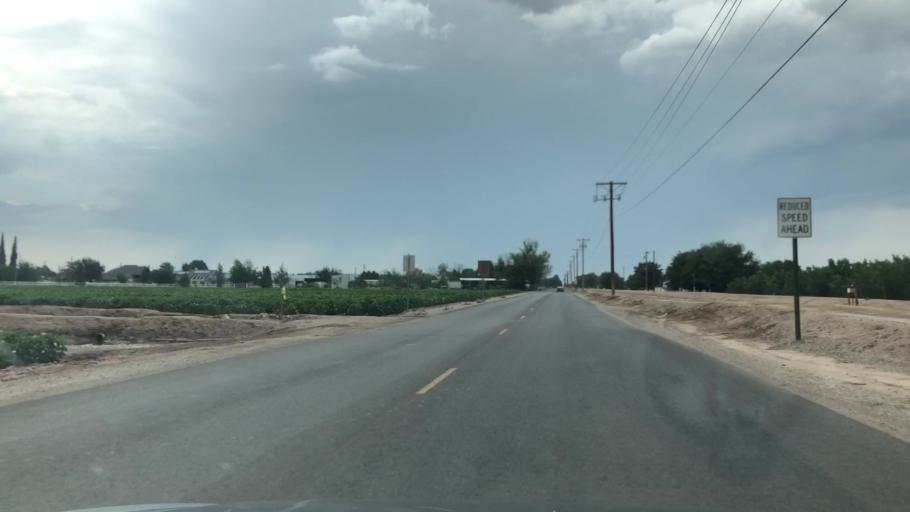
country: US
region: Texas
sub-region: El Paso County
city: Canutillo
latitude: 31.9111
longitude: -106.6249
